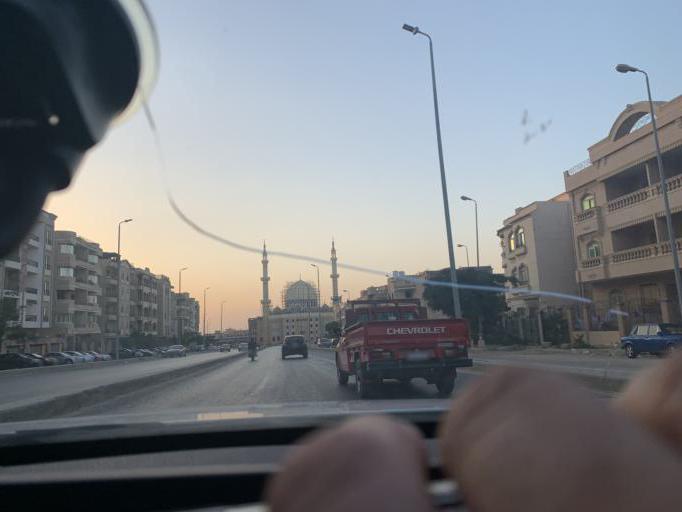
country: EG
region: Muhafazat al Qahirah
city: Cairo
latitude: 30.0035
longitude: 31.4591
